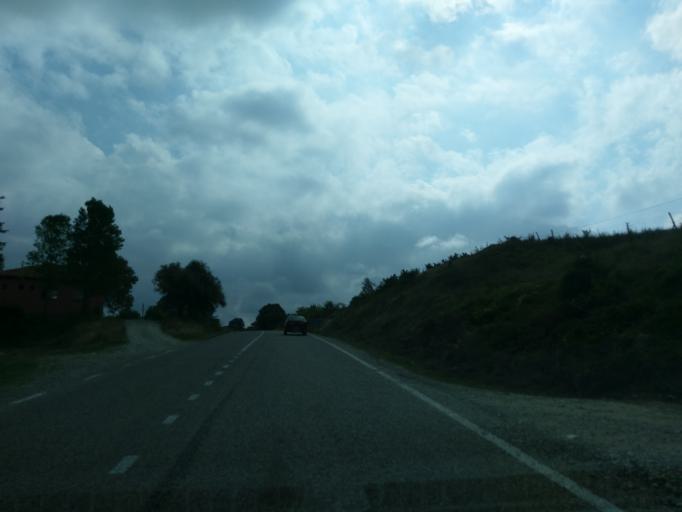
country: TR
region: Sinop
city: Erfelek
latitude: 41.9656
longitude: 34.8458
